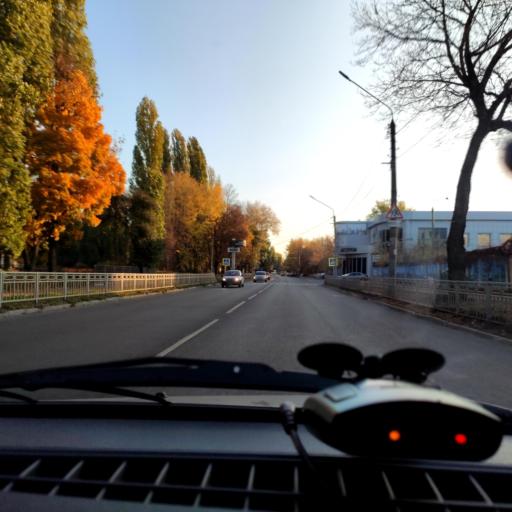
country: RU
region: Voronezj
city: Voronezh
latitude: 51.6809
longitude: 39.1940
